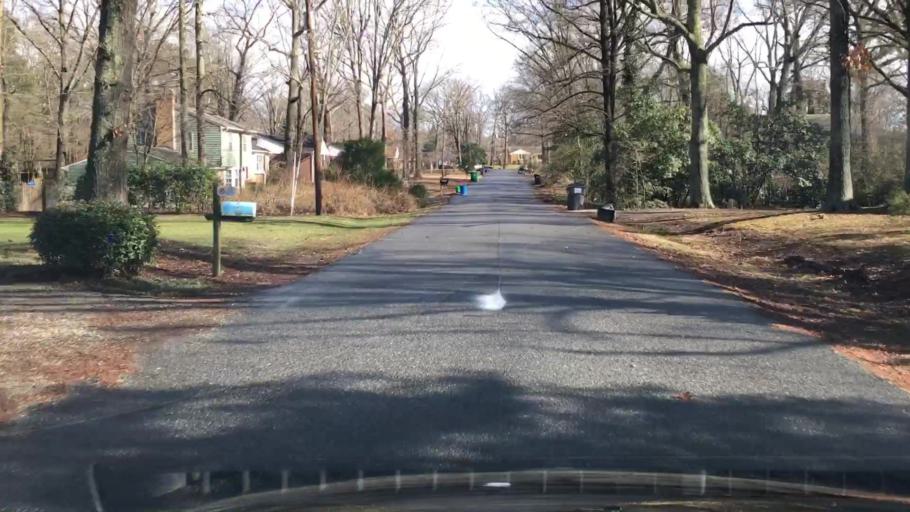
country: US
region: Virginia
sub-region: Chesterfield County
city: Bon Air
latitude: 37.5317
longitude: -77.5853
